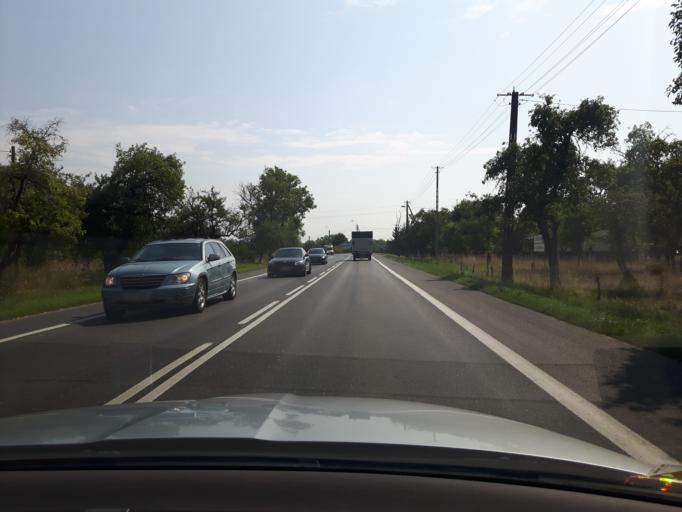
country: PL
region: Masovian Voivodeship
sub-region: Powiat mlawski
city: Wisniewo
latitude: 53.0042
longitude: 20.3293
